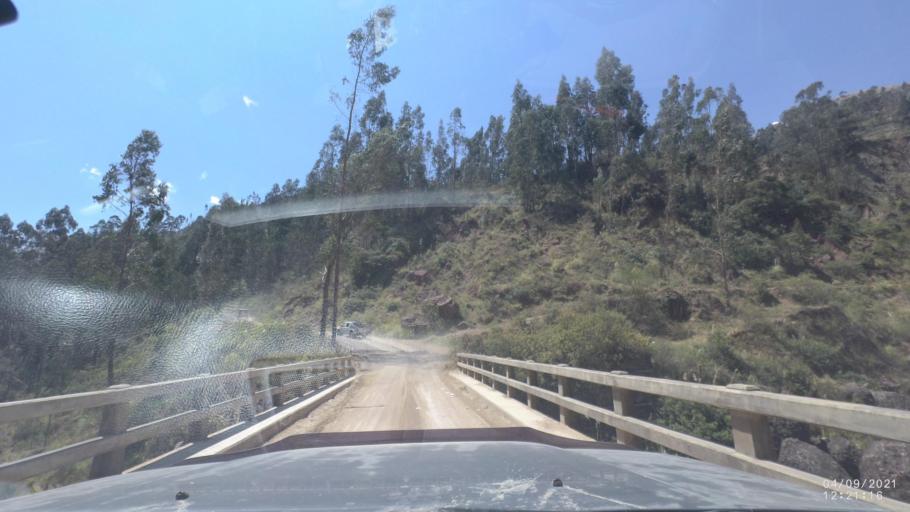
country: BO
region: Cochabamba
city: Colchani
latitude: -17.2408
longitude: -66.5268
